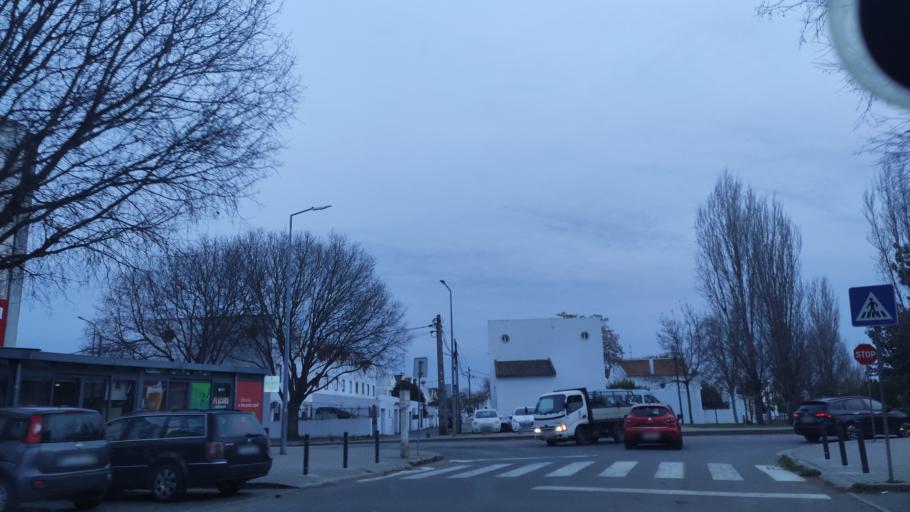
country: PT
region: Beja
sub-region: Beja
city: Beja
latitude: 38.0196
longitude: -7.8524
